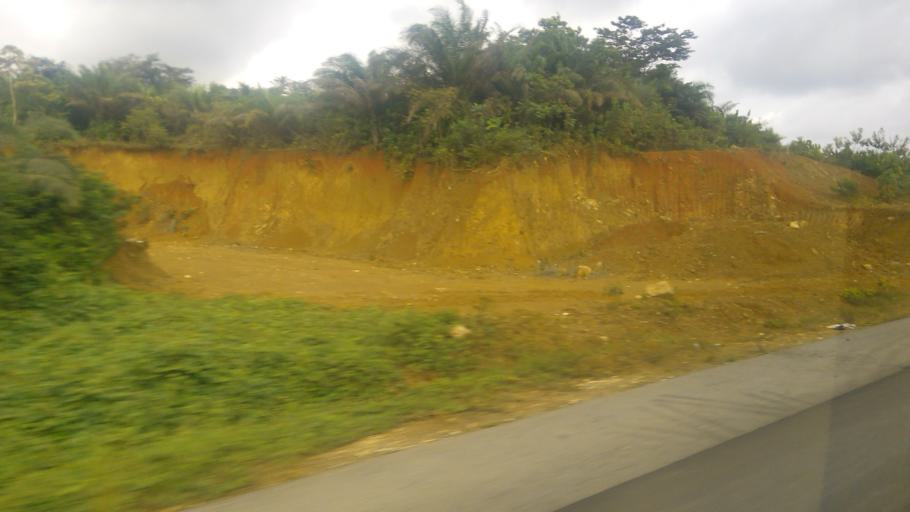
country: GH
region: Western
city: Axim
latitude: 4.8948
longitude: -2.2320
